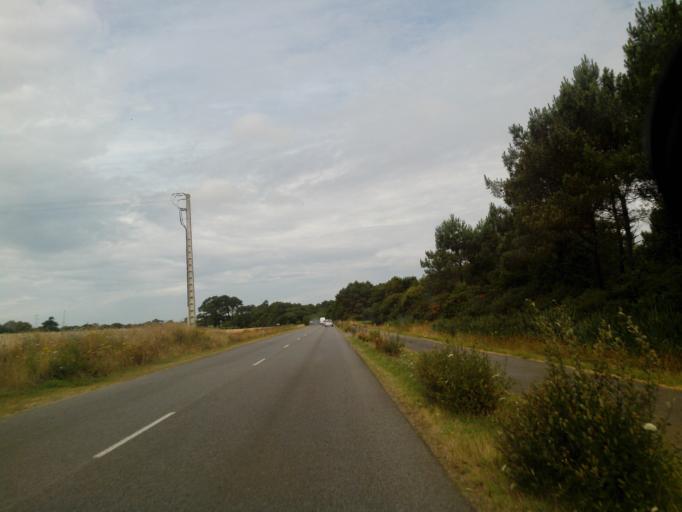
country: FR
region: Brittany
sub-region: Departement du Morbihan
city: Erdeven
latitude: 47.6431
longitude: -3.1232
